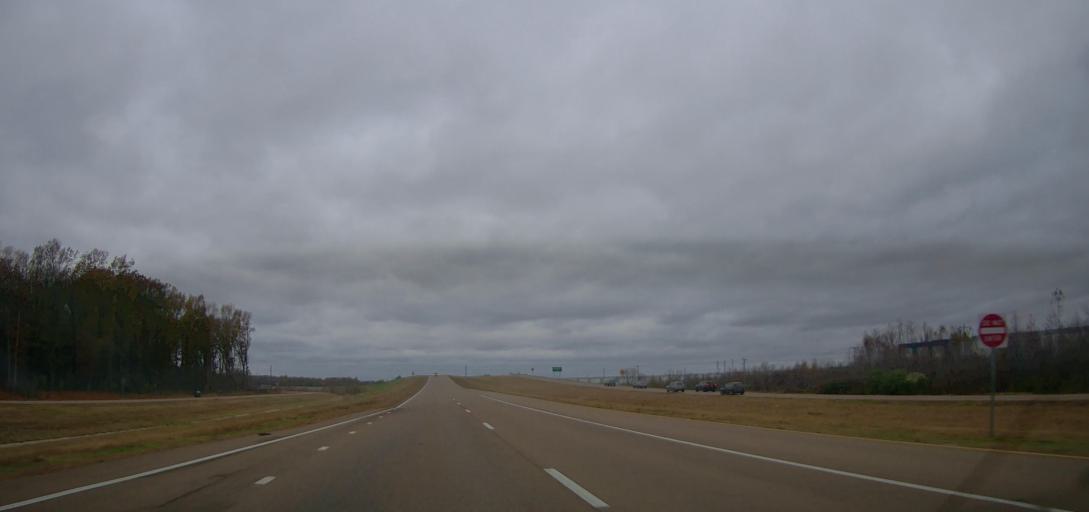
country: US
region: Tennessee
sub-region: Fayette County
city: Piperton
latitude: 34.9839
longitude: -89.5916
